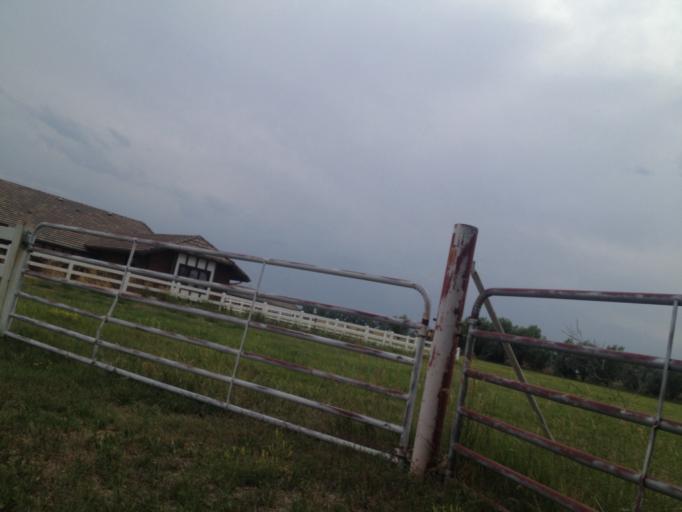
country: US
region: Colorado
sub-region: Boulder County
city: Louisville
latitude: 39.9525
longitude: -105.1358
